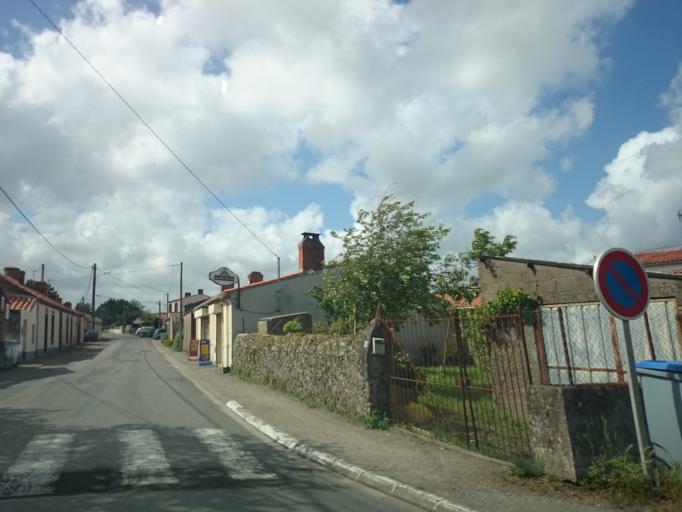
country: FR
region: Pays de la Loire
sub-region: Departement de la Loire-Atlantique
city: Bouaye
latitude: 47.1366
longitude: -1.6693
